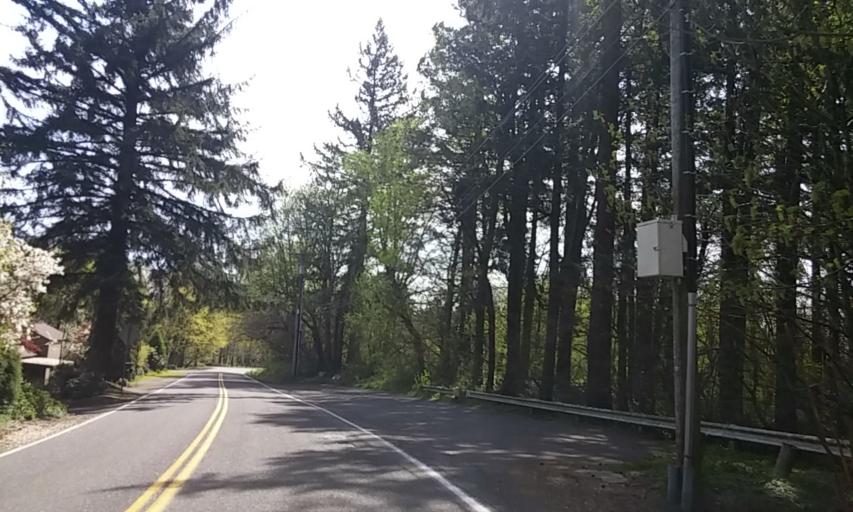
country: US
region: Oregon
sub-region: Washington County
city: West Haven-Sylvan
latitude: 45.5213
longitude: -122.7439
